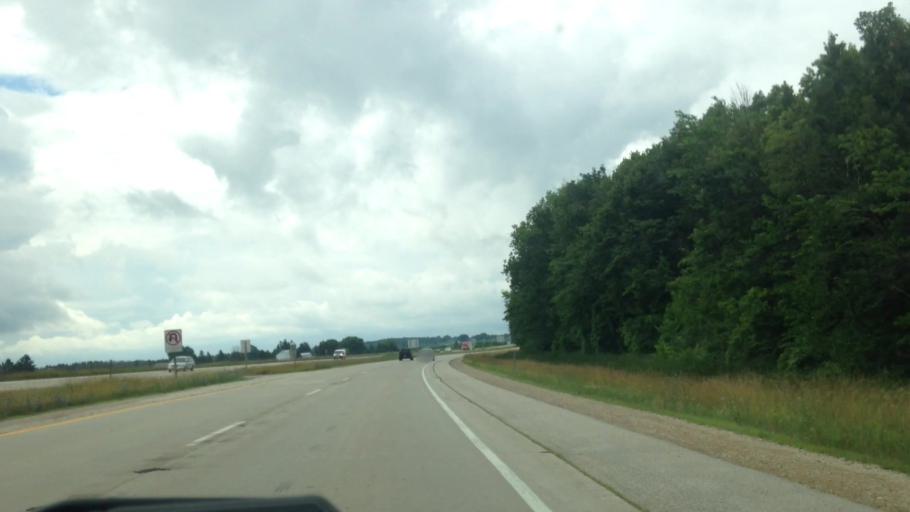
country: US
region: Wisconsin
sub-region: Washington County
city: Jackson
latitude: 43.3181
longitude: -88.1847
